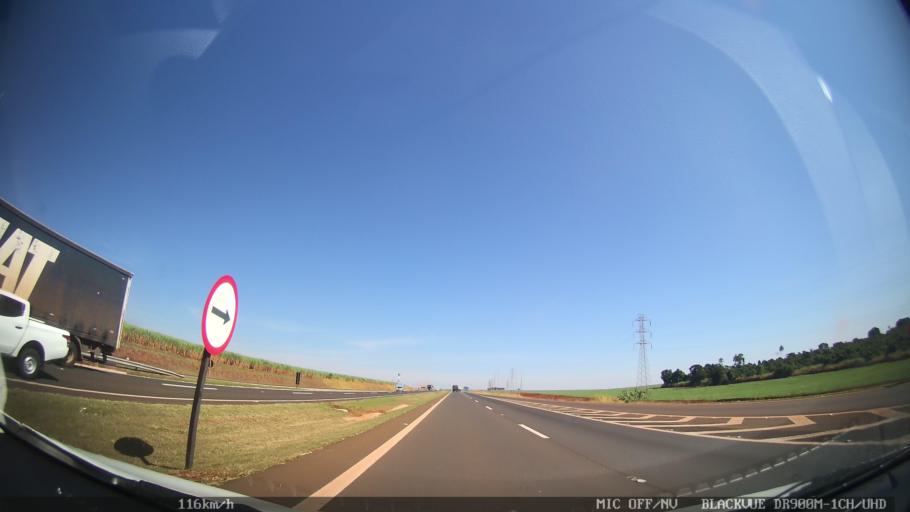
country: BR
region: Sao Paulo
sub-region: Ribeirao Preto
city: Ribeirao Preto
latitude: -21.1496
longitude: -47.8834
